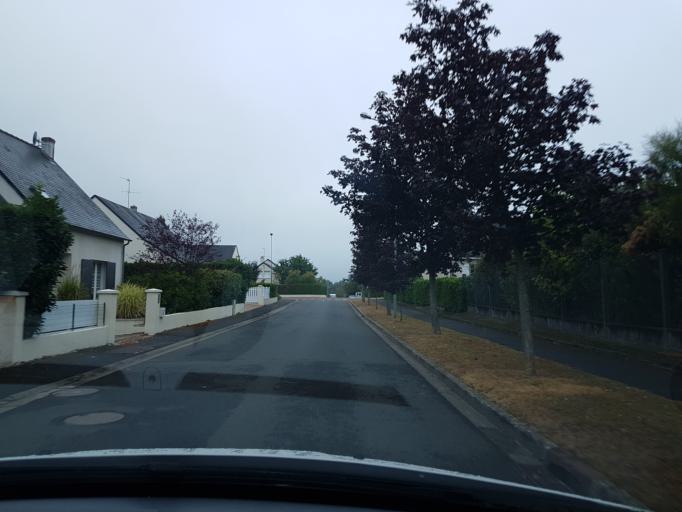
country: FR
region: Centre
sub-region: Departement d'Indre-et-Loire
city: Saint-Avertin
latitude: 47.3621
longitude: 0.7428
